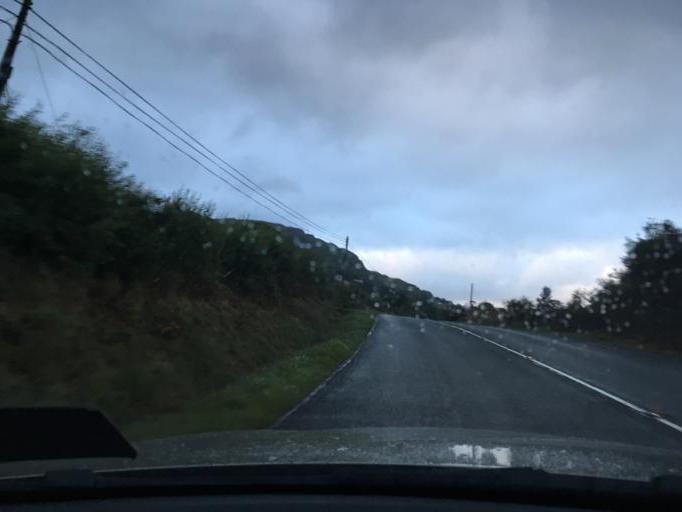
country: IE
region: Ulster
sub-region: County Donegal
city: Killybegs
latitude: 54.6354
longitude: -8.4954
